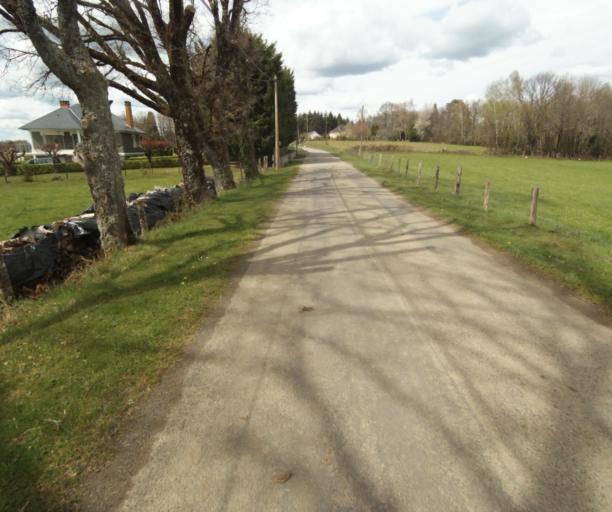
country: FR
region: Limousin
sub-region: Departement de la Correze
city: Laguenne
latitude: 45.2271
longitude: 1.8795
